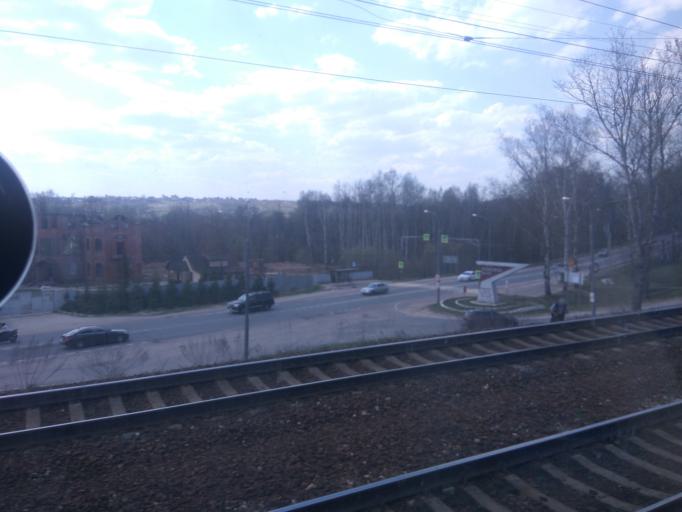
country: RU
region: Moskovskaya
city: Yakhroma
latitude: 56.3006
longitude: 37.4946
